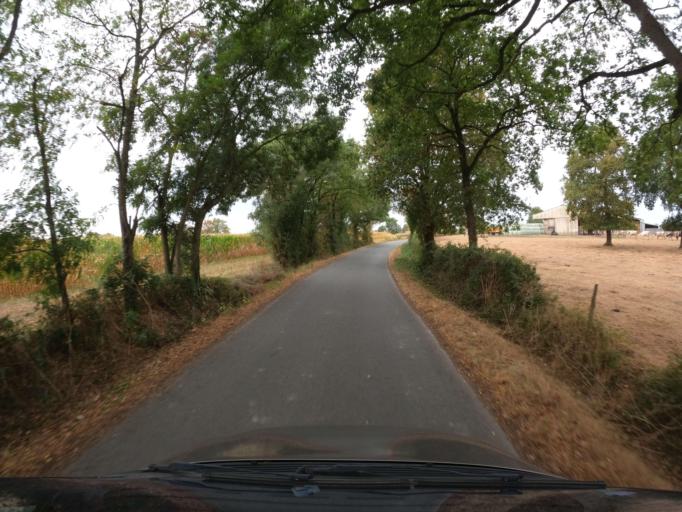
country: FR
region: Pays de la Loire
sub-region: Departement de la Vendee
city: La Boissiere-de-Montaigu
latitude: 46.9831
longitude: -1.1679
